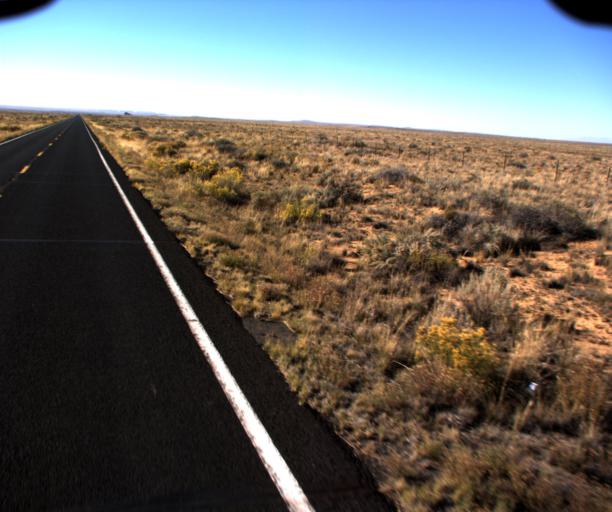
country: US
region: Arizona
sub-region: Navajo County
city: First Mesa
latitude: 35.7671
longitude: -110.5078
